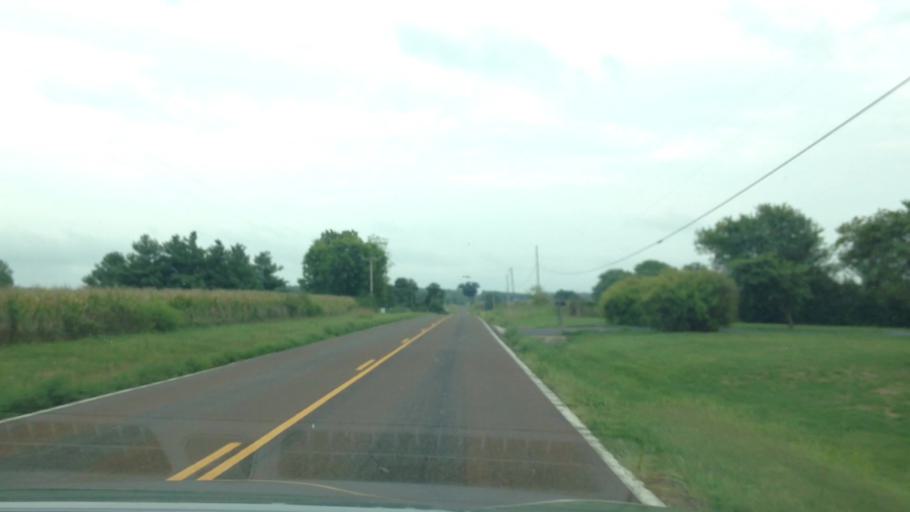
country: US
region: Missouri
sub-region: Clay County
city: Smithville
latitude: 39.4050
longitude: -94.6185
